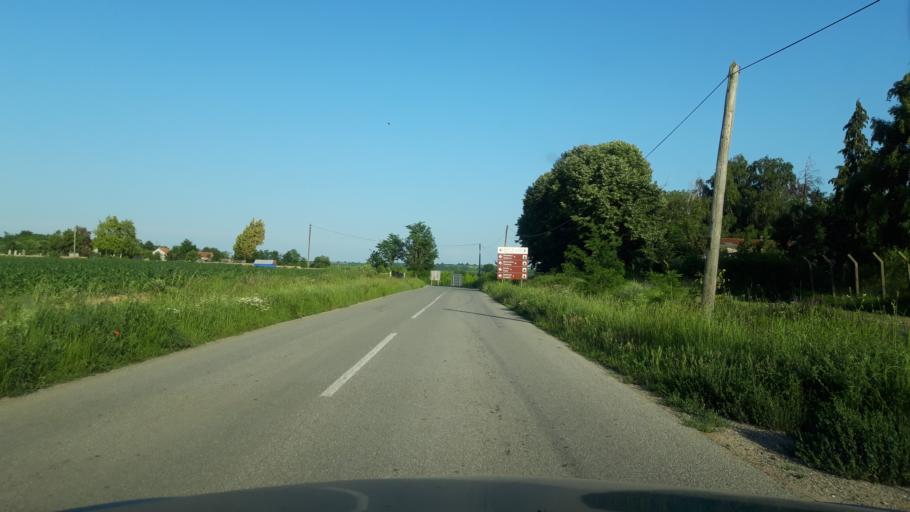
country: RS
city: Macvanska Mitrovica
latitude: 45.1037
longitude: 19.5000
